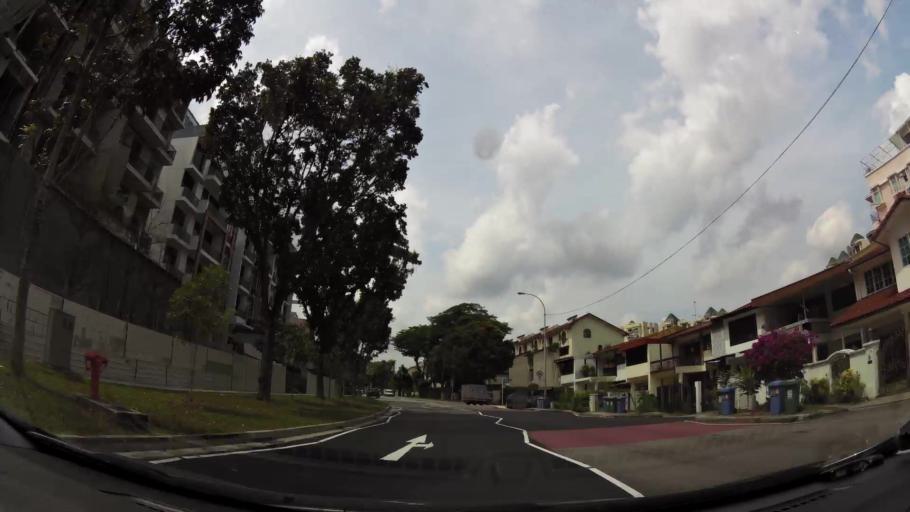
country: SG
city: Singapore
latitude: 1.3403
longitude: 103.7701
